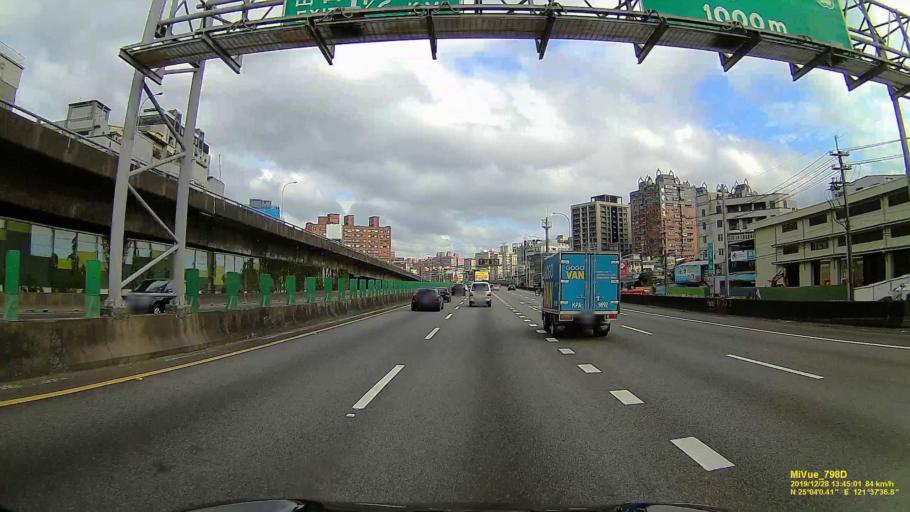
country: TW
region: Taipei
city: Taipei
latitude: 25.0668
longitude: 121.6272
